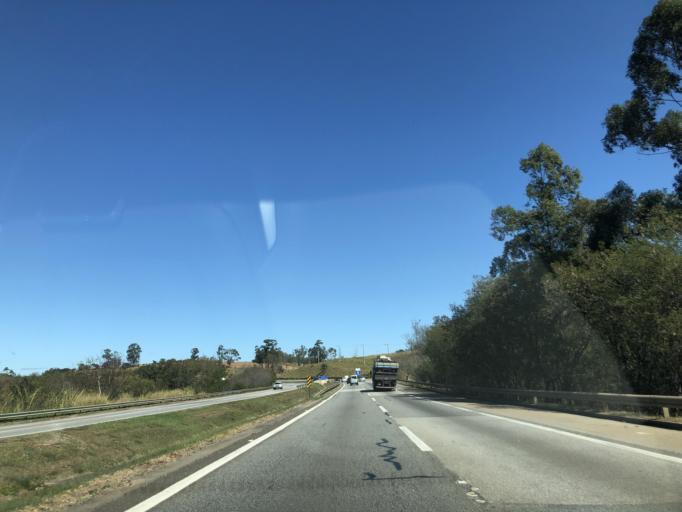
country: BR
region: Sao Paulo
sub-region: Sorocaba
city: Sorocaba
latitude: -23.4650
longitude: -47.3817
